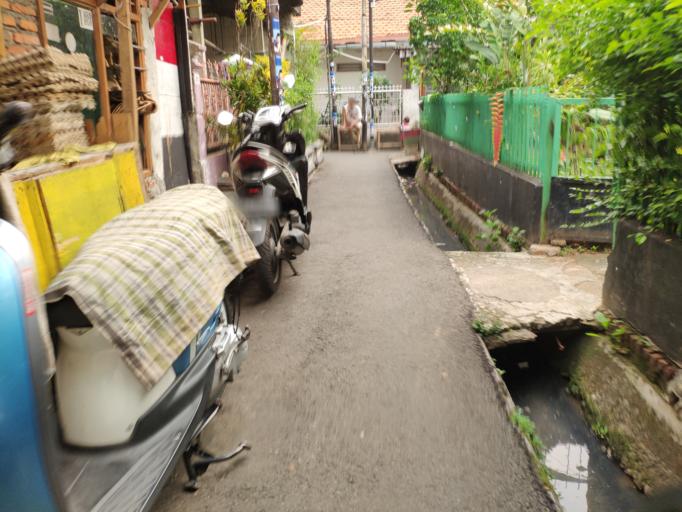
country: ID
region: Jakarta Raya
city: Jakarta
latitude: -6.1951
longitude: 106.8638
